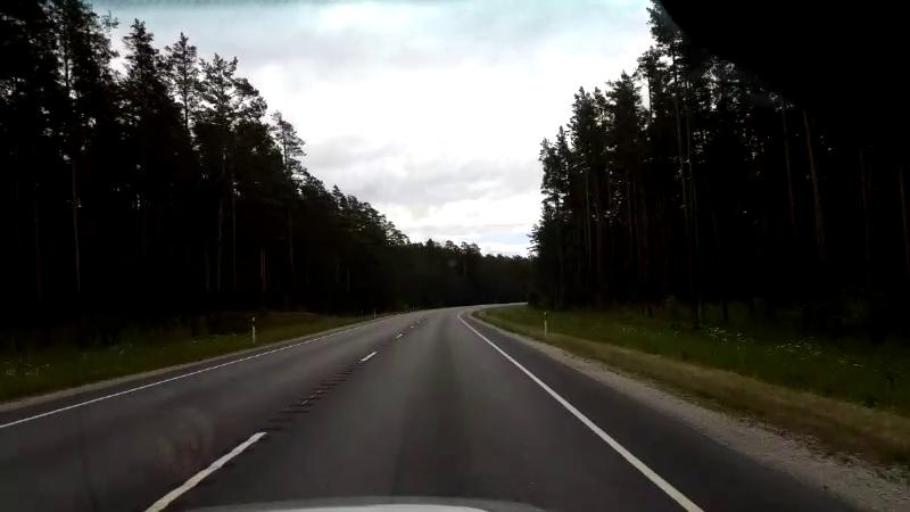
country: EE
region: Paernumaa
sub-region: Paernu linn
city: Parnu
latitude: 58.1420
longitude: 24.5064
